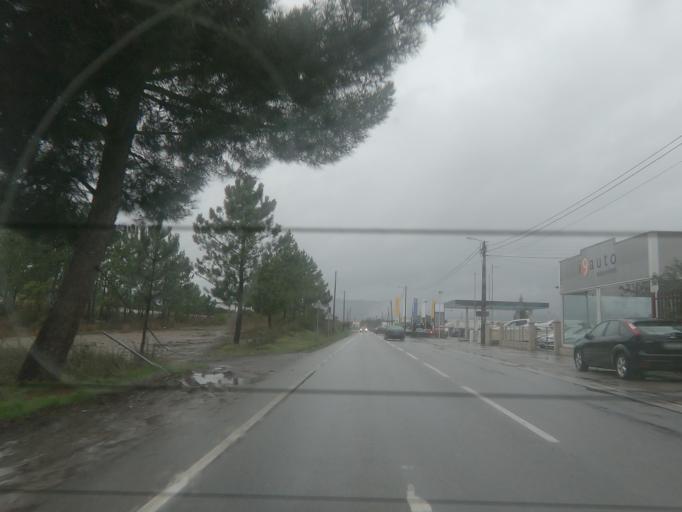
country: PT
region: Vila Real
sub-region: Vila Real
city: Vila Real
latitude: 41.2751
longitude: -7.7142
